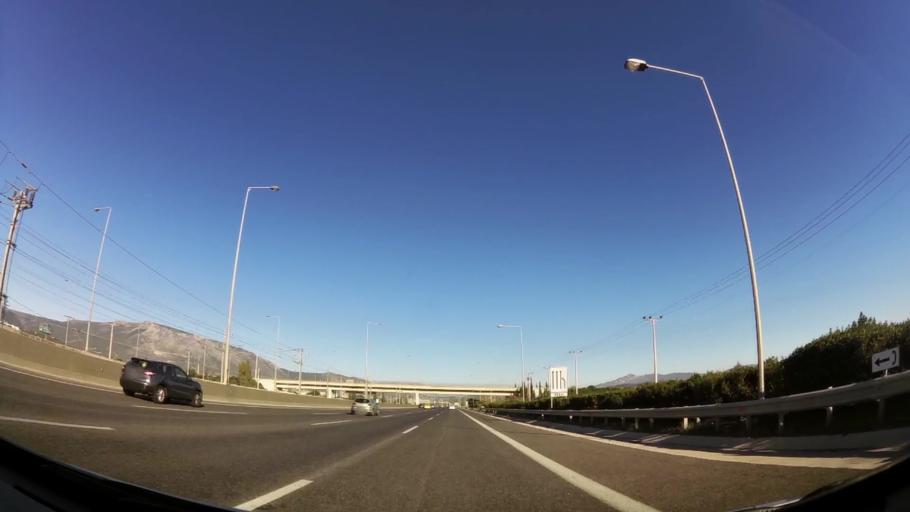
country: GR
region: Attica
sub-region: Nomarchia Anatolikis Attikis
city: Koropi
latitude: 37.9171
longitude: 23.8936
